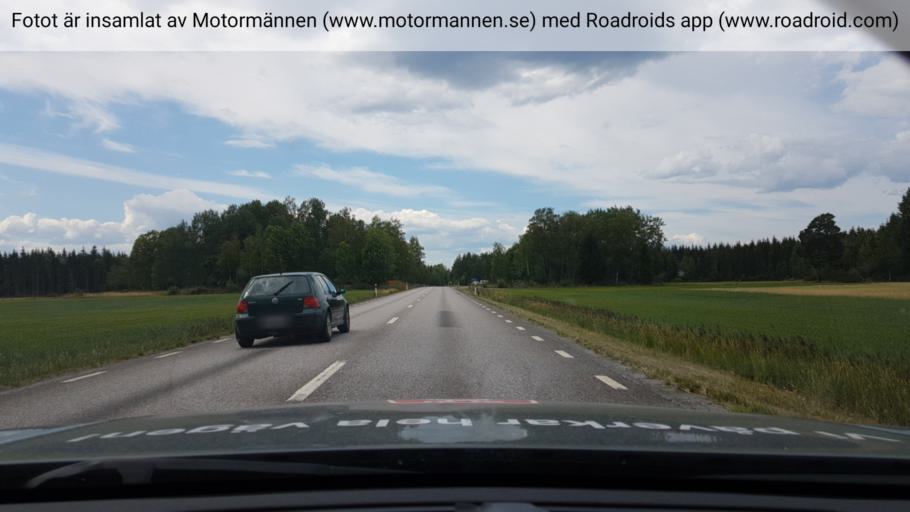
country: SE
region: Vaestmanland
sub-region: Sala Kommun
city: Sala
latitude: 59.8351
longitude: 16.6915
